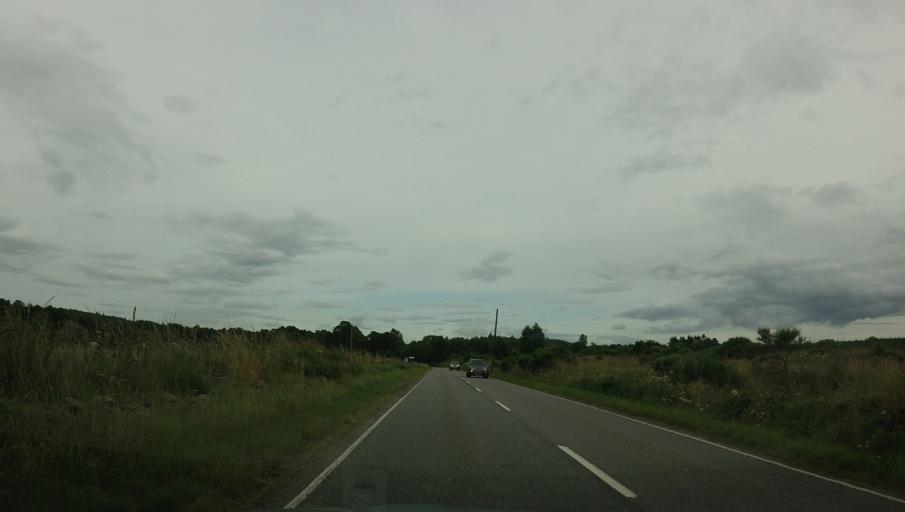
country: GB
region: Scotland
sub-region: Aberdeenshire
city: Aboyne
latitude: 57.0868
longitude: -2.7298
